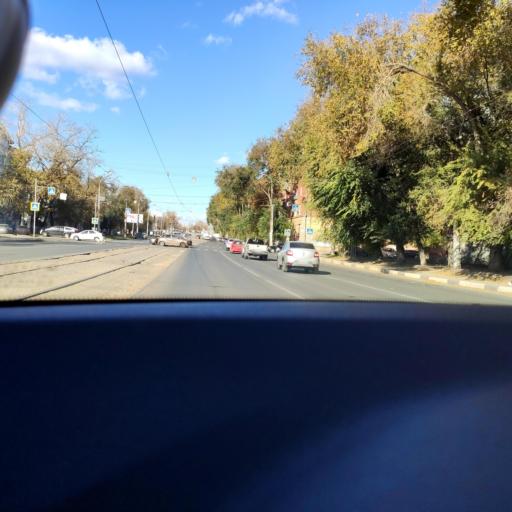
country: RU
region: Samara
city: Samara
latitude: 53.2155
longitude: 50.2678
